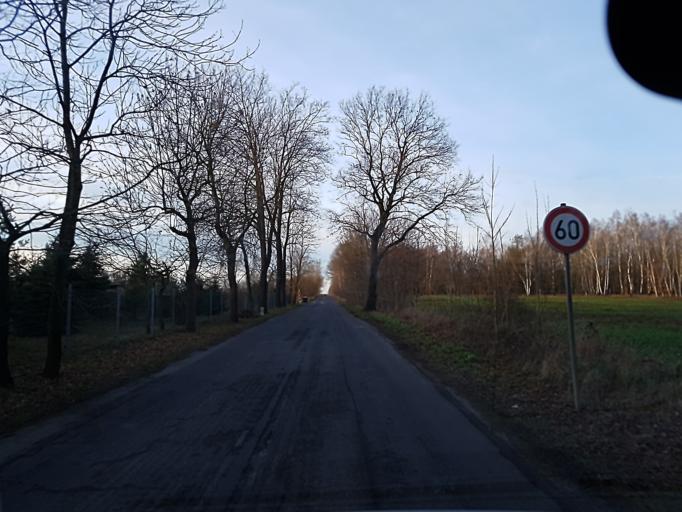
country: DE
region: Brandenburg
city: Finsterwalde
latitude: 51.6002
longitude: 13.7304
